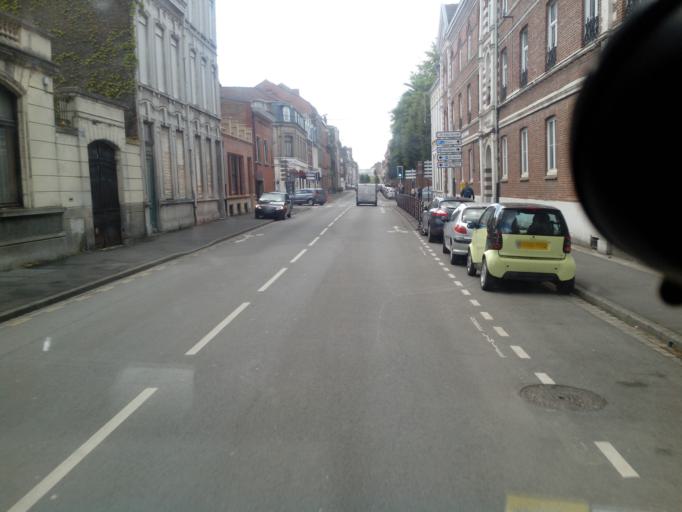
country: FR
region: Nord-Pas-de-Calais
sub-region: Departement du Nord
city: Armentieres
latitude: 50.6862
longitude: 2.8780
